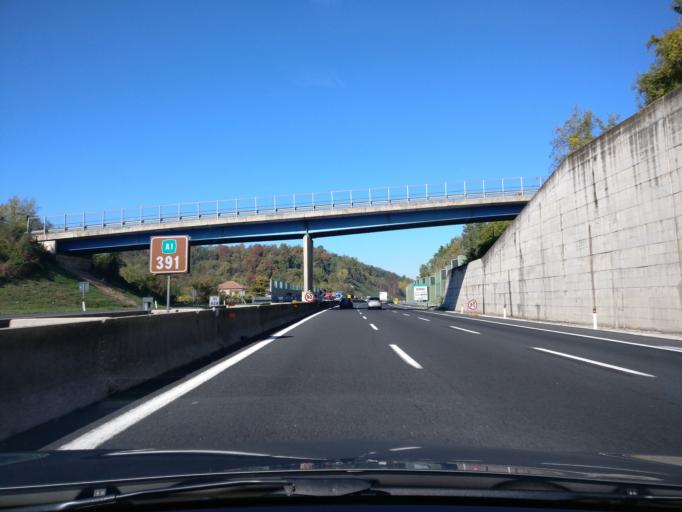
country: IT
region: Latium
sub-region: Provincia di Frosinone
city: Ceccano
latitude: 41.5914
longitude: 13.3413
